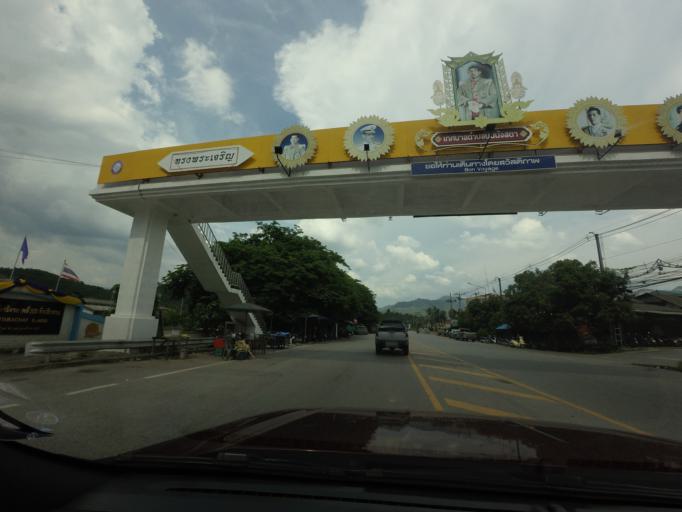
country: TH
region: Yala
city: Ban Nang Sata
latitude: 6.2668
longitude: 101.2655
